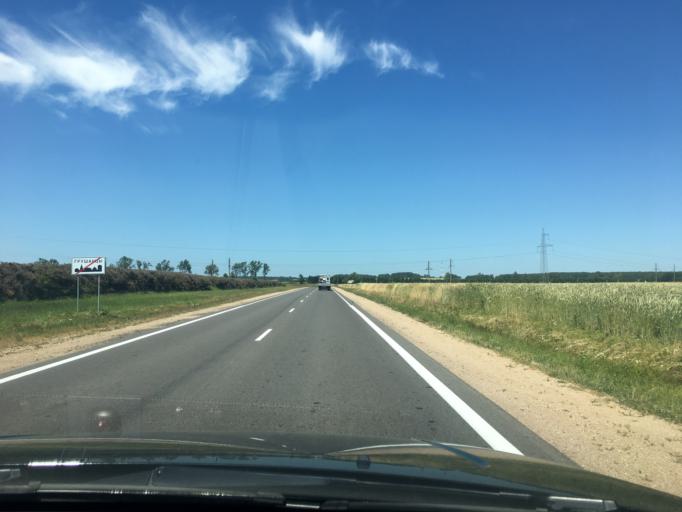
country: BY
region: Grodnenskaya
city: Hal'shany
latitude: 54.1021
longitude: 25.9129
